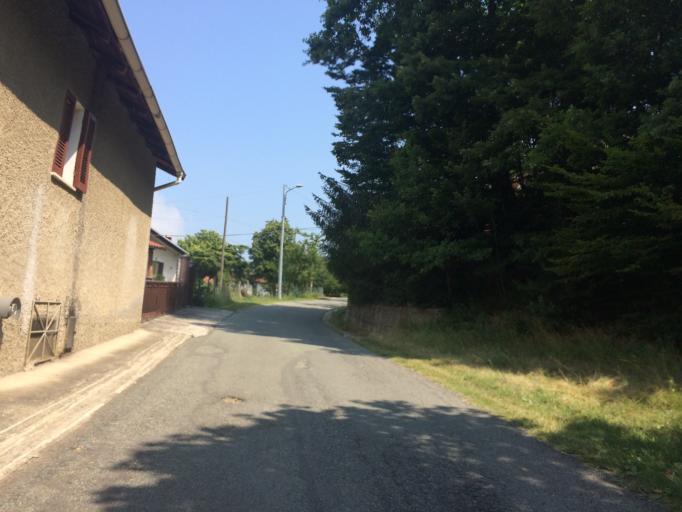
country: IT
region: Liguria
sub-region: Provincia di Savona
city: Molino-Pera
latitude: 44.4758
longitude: 8.3519
